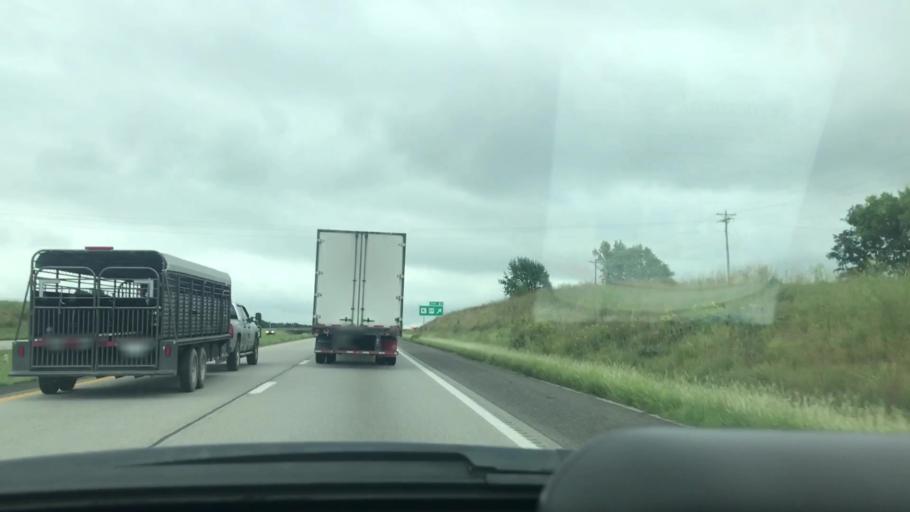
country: US
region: Missouri
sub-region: Greene County
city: Republic
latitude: 37.1859
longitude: -93.5746
